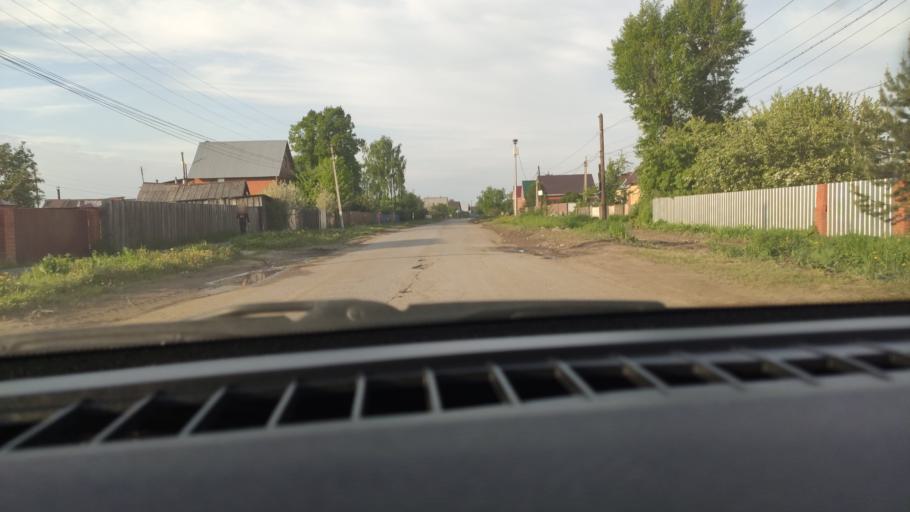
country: RU
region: Perm
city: Kultayevo
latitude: 57.9334
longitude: 56.0200
